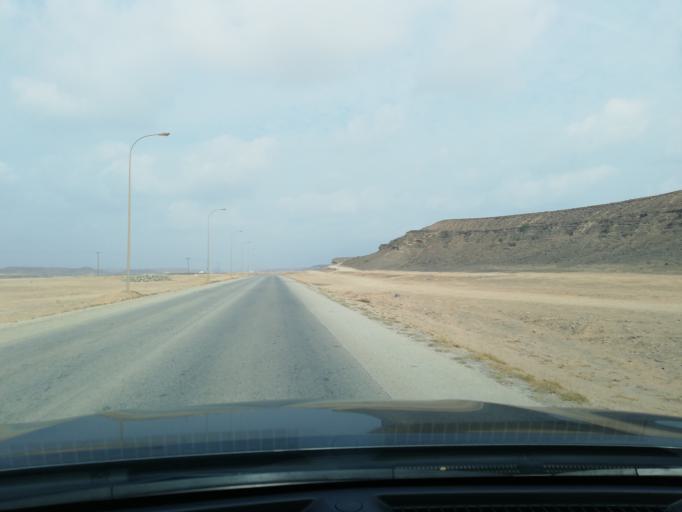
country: OM
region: Zufar
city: Salalah
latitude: 16.9524
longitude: 53.9262
